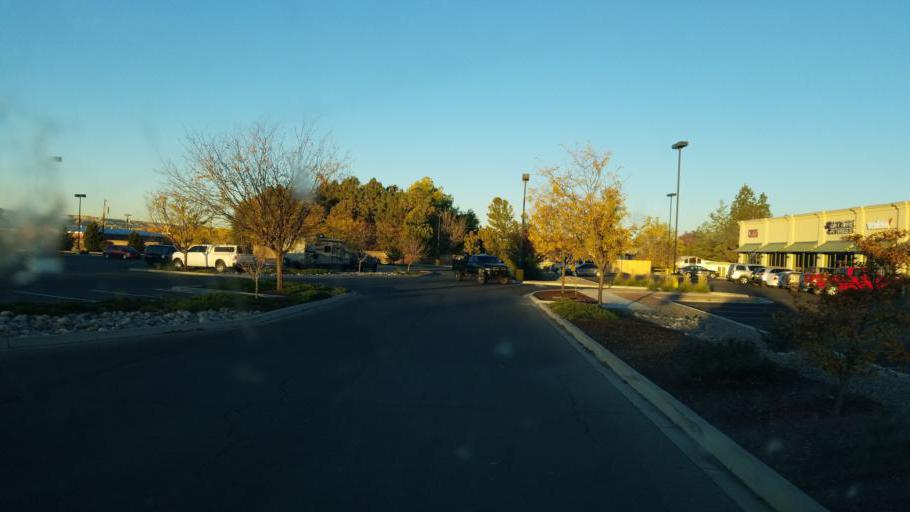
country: US
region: New Mexico
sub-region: San Juan County
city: Farmington
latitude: 36.7331
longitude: -108.2281
